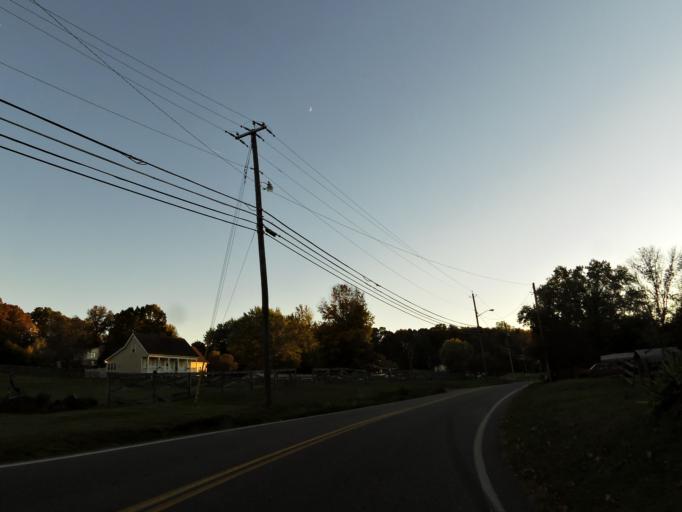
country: US
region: Tennessee
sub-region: Knox County
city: Knoxville
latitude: 36.0257
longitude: -83.9729
